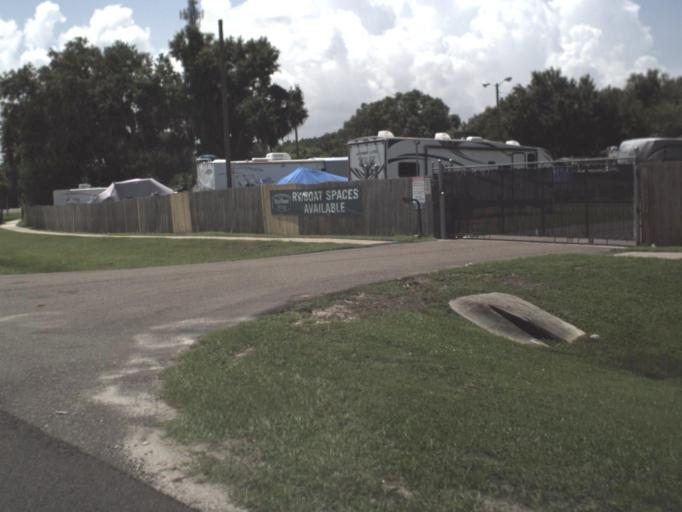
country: US
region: Florida
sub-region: Hillsborough County
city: Riverview
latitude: 27.8838
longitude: -82.3274
